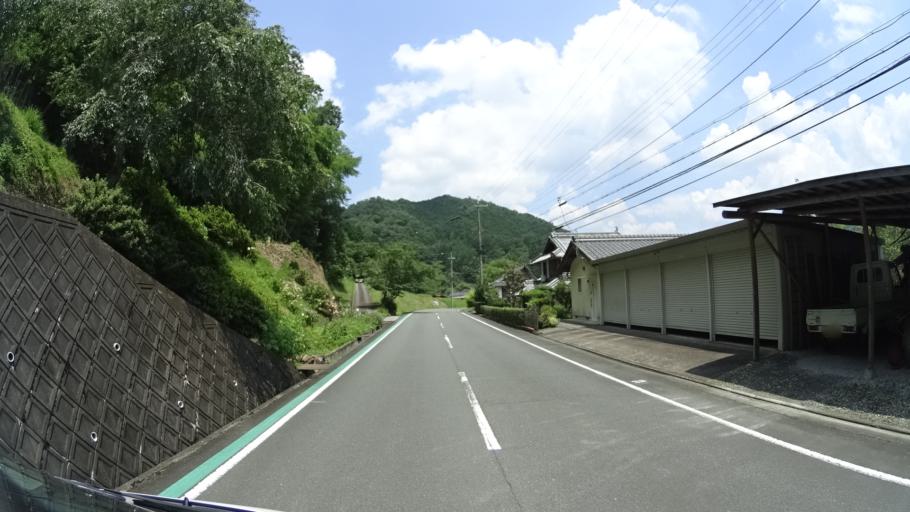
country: JP
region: Kyoto
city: Ayabe
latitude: 35.2089
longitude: 135.2270
